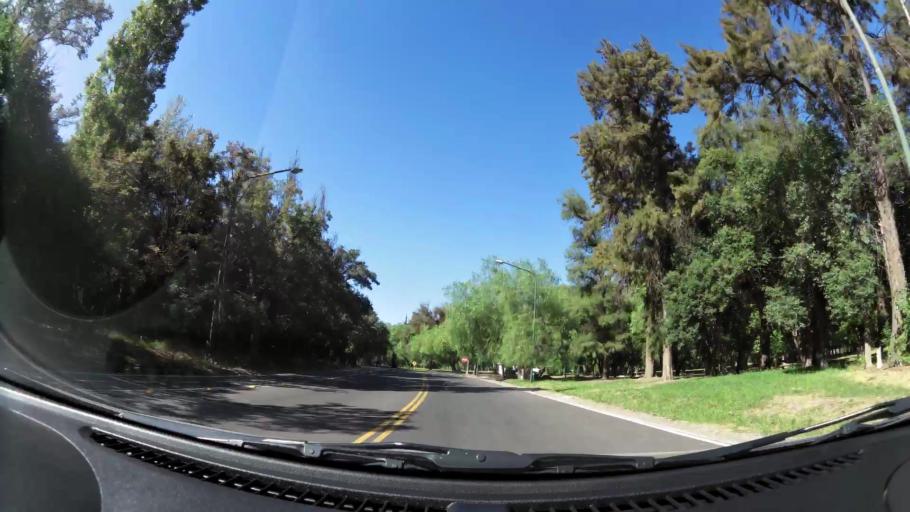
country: AR
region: Mendoza
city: Mendoza
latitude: -32.8909
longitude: -68.8733
